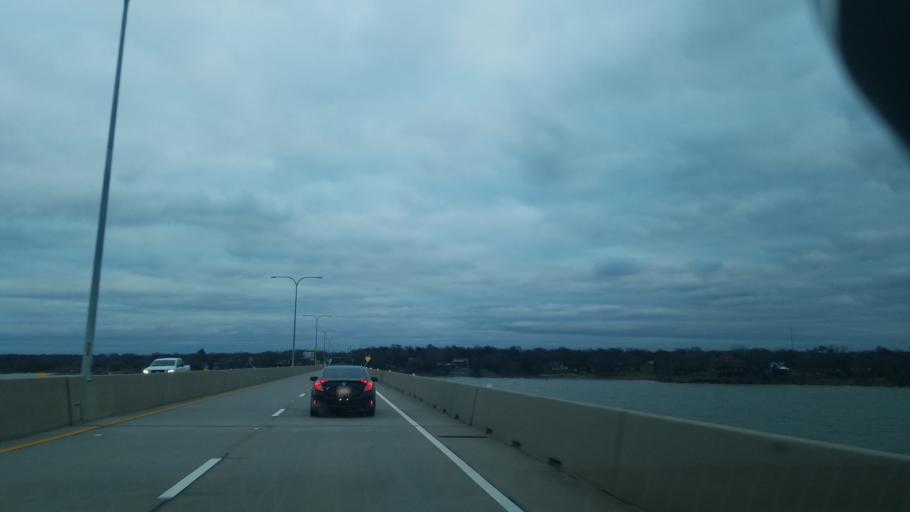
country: US
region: Texas
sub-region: Denton County
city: Lake Dallas
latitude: 33.1400
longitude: -96.9961
